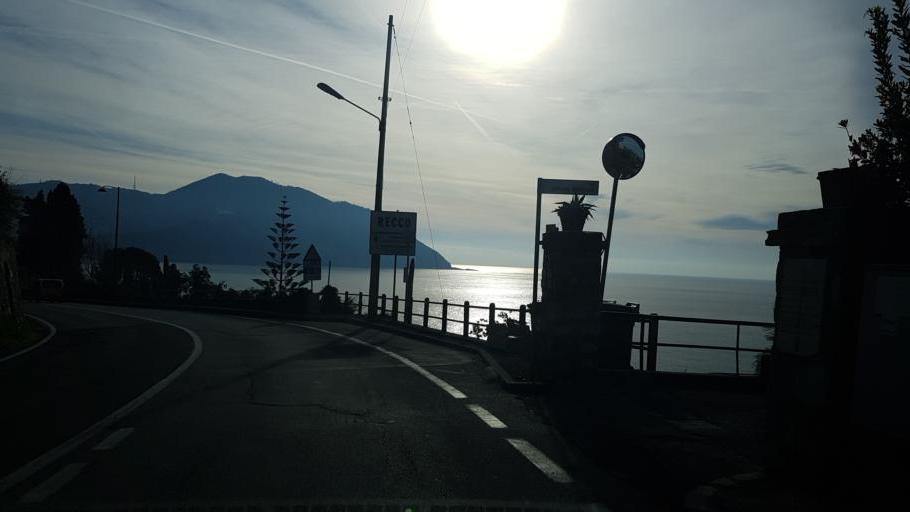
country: IT
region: Liguria
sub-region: Provincia di Genova
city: Recco
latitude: 44.3647
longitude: 9.1239
